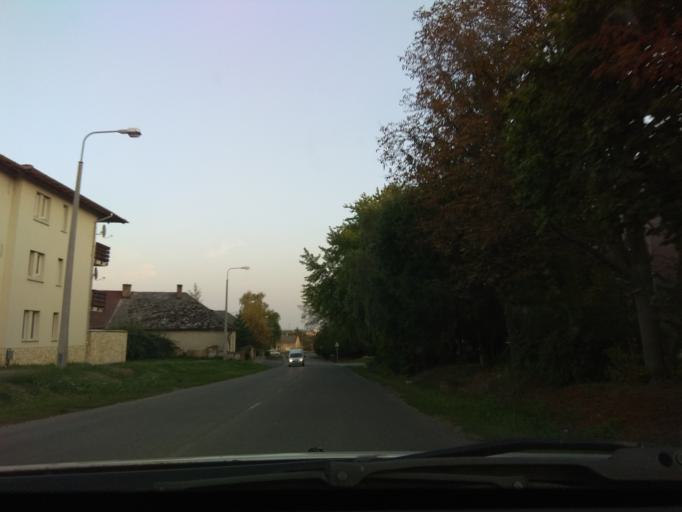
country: HU
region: Borsod-Abauj-Zemplen
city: Szerencs
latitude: 48.1653
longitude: 21.2057
